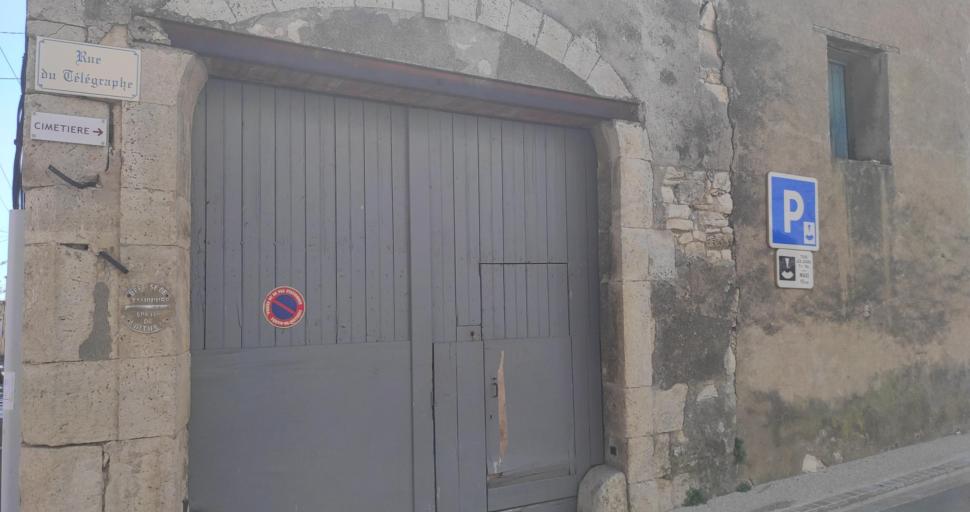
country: FR
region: Languedoc-Roussillon
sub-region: Departement de l'Aude
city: Peyriac-de-Mer
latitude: 43.0864
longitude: 2.9601
